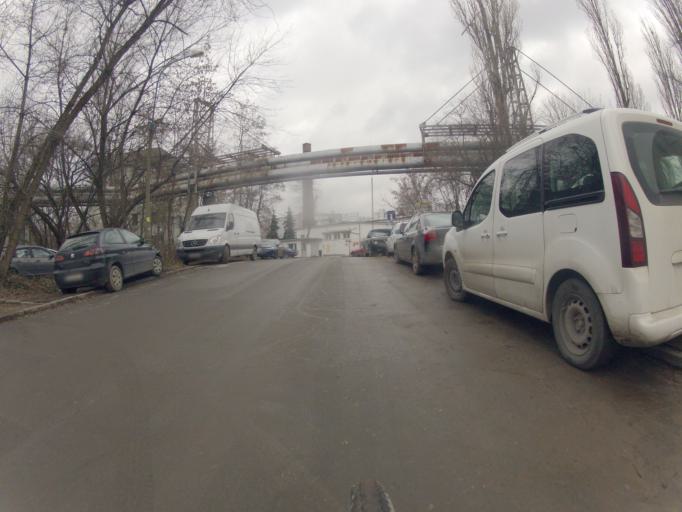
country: PL
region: Lesser Poland Voivodeship
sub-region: Krakow
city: Krakow
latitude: 50.0641
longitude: 19.9738
